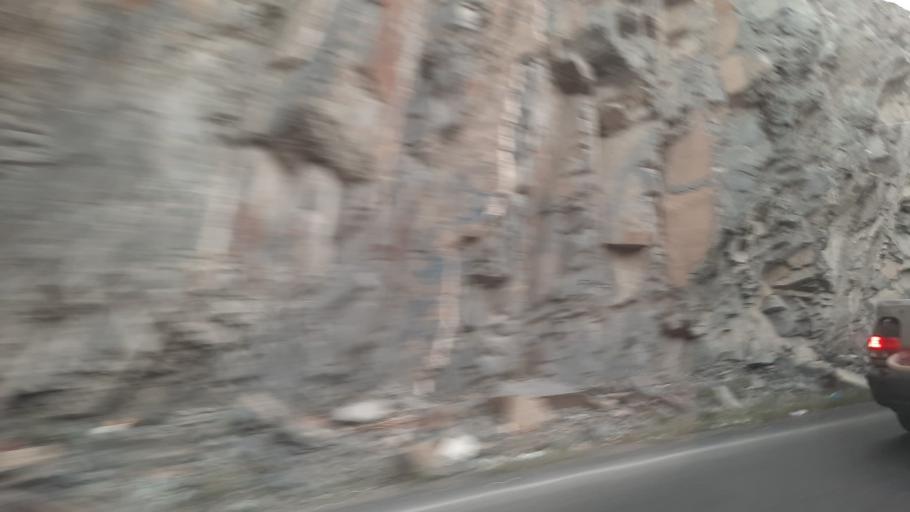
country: IR
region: Markazi
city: Arak
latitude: 34.0413
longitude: 49.5982
